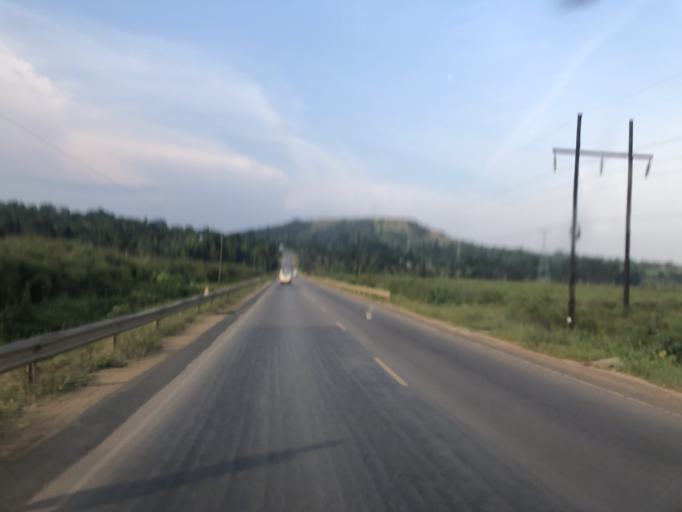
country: UG
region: Central Region
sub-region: Mpigi District
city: Mpigi
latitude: 0.1851
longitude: 32.2872
